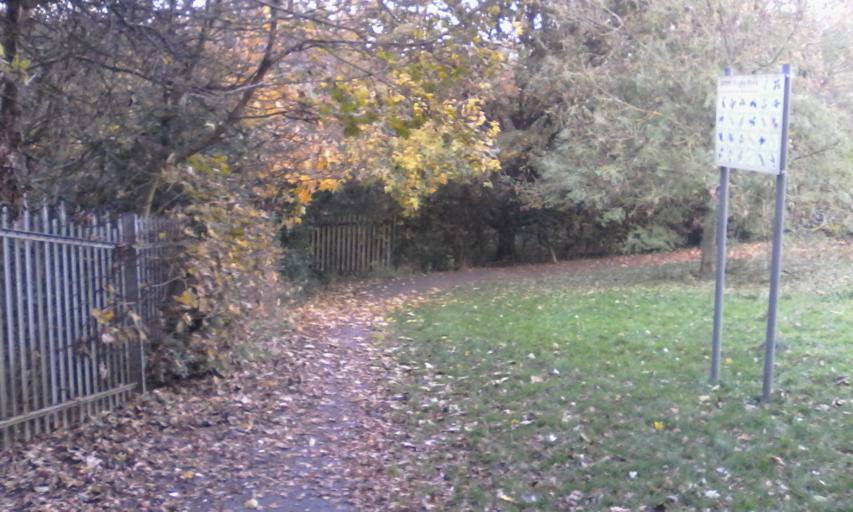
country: GB
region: England
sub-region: Nottinghamshire
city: Arnold
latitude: 52.9840
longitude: -1.1084
